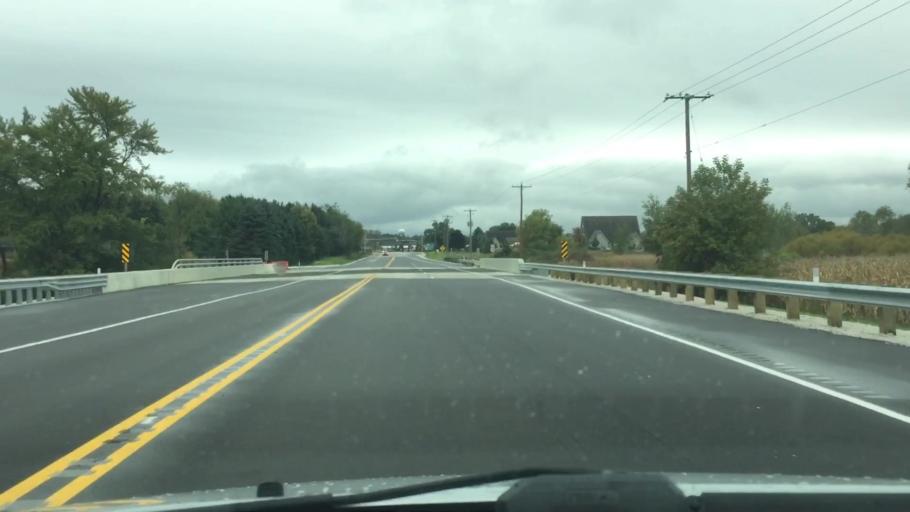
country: US
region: Wisconsin
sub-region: Waukesha County
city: Dousman
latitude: 43.0263
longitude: -88.4624
